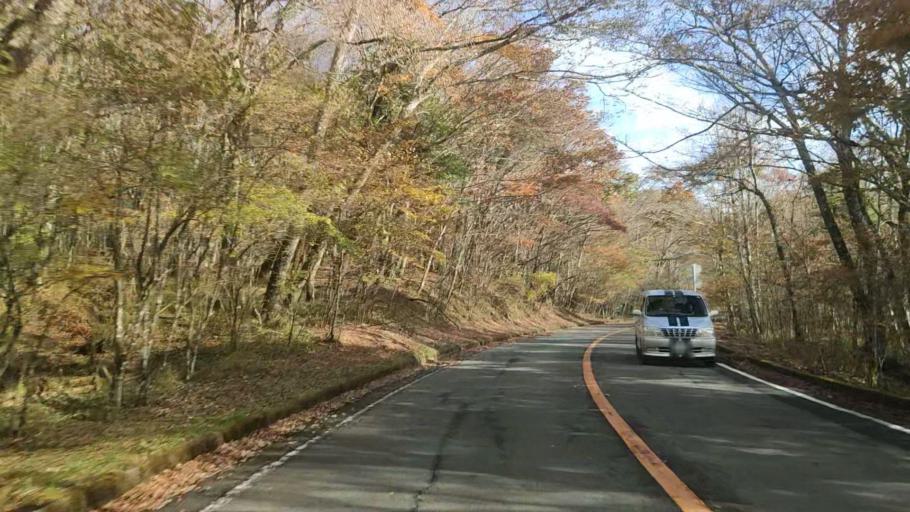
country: JP
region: Shizuoka
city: Fujinomiya
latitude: 35.2962
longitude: 138.7049
